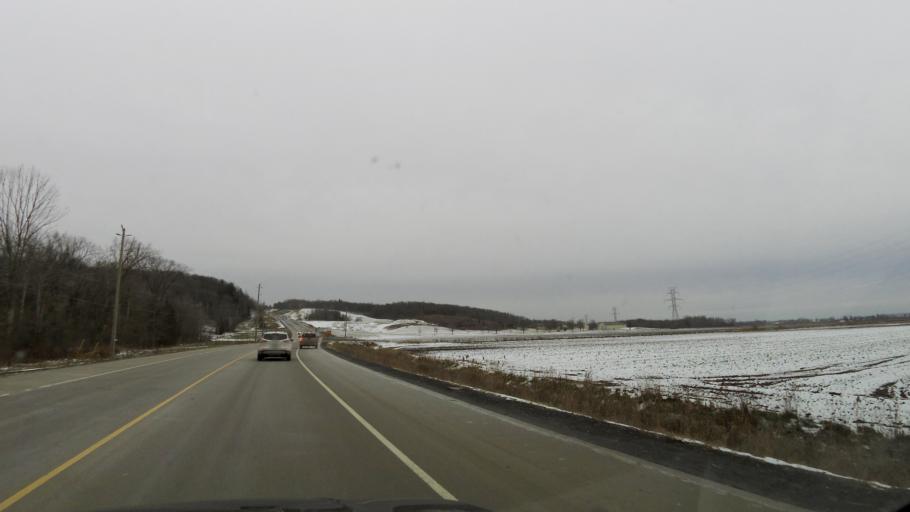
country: CA
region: Ontario
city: Newmarket
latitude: 44.0939
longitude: -79.5176
